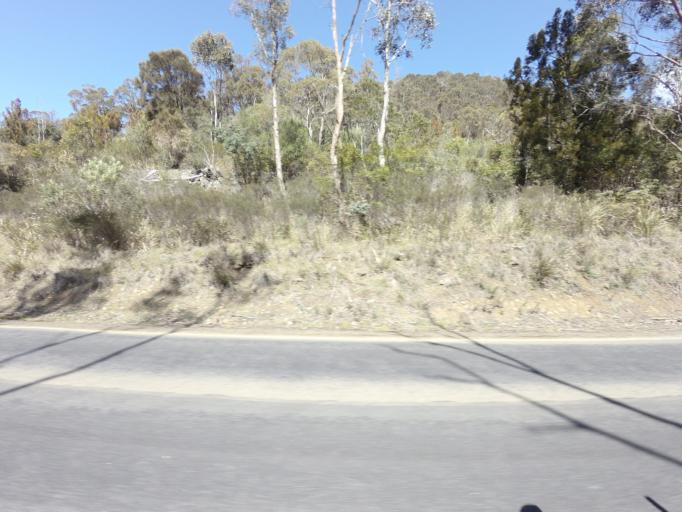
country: AU
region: Tasmania
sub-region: Derwent Valley
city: New Norfolk
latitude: -42.6771
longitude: 146.7572
